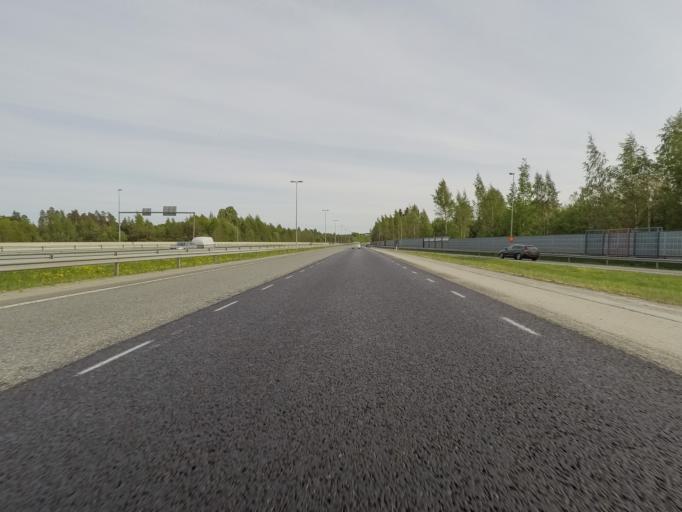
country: FI
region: Haeme
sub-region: Haemeenlinna
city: Haemeenlinna
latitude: 60.9686
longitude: 24.4751
